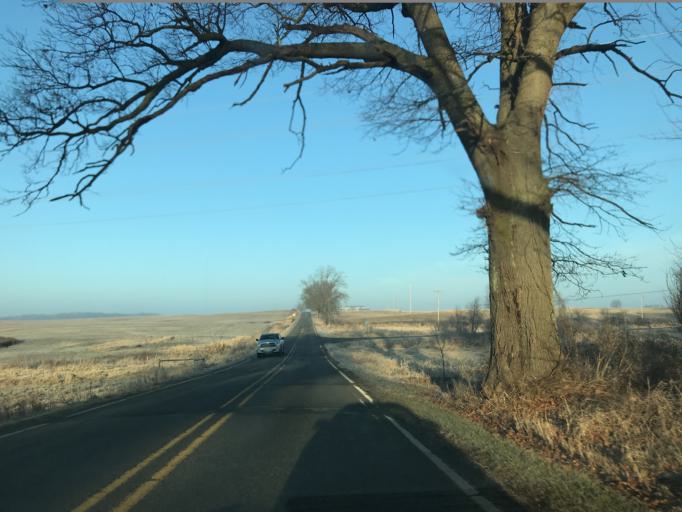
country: US
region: Michigan
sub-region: Ingham County
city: Leslie
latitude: 42.4101
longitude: -84.4960
